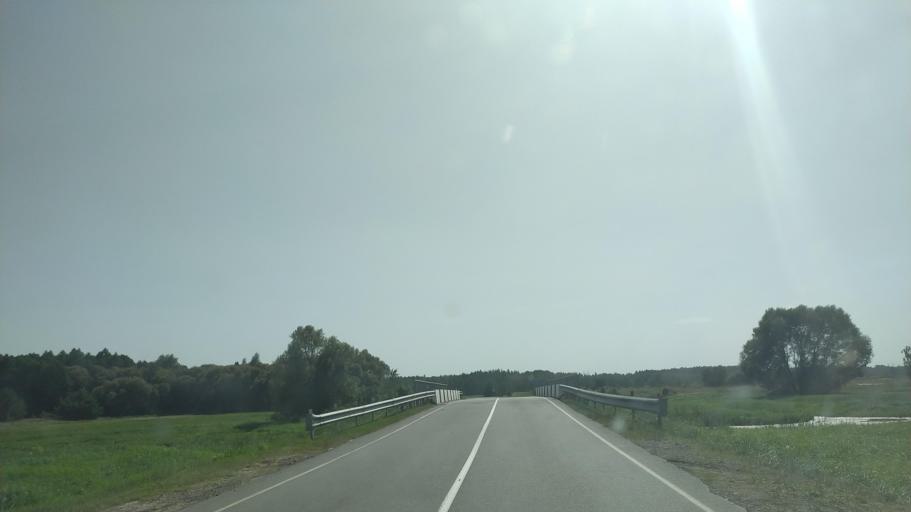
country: BY
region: Brest
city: Byaroza
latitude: 52.4194
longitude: 24.9804
